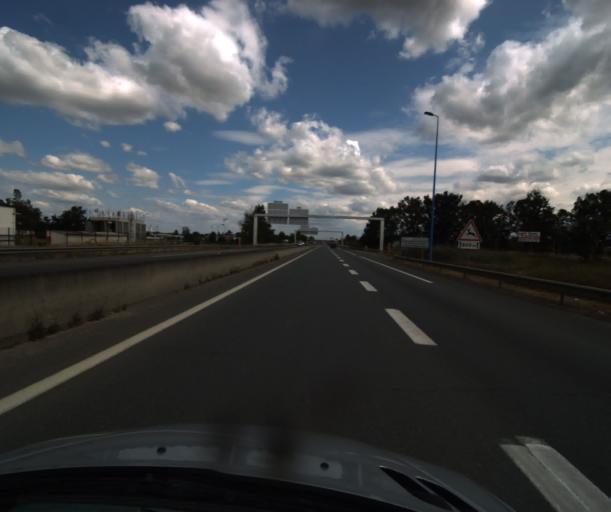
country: FR
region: Midi-Pyrenees
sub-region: Departement du Tarn-et-Garonne
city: Campsas
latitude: 43.9322
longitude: 1.3193
